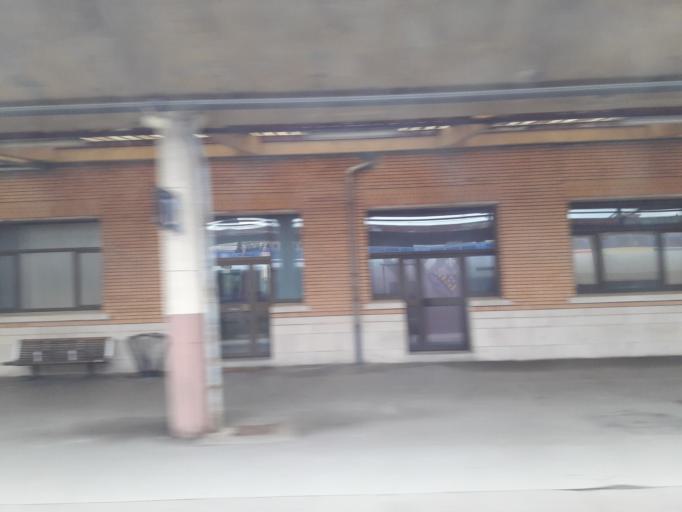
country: FR
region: Franche-Comte
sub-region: Territoire de Belfort
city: Belfort
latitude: 47.6325
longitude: 6.8540
